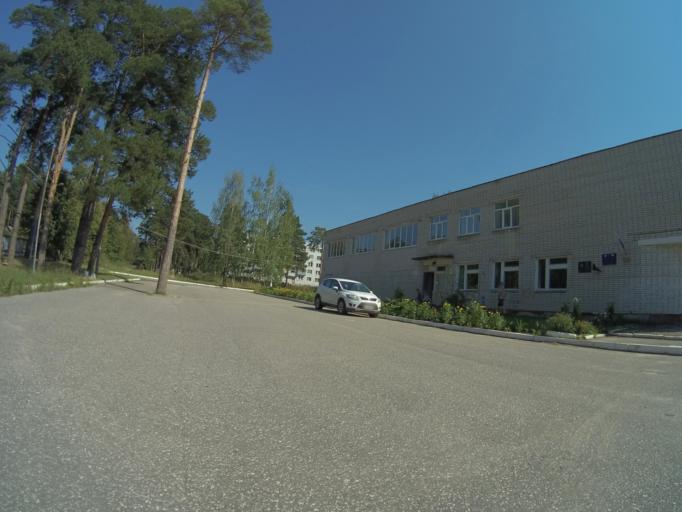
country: RU
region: Vladimir
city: Bogolyubovo
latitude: 56.2536
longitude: 40.5495
